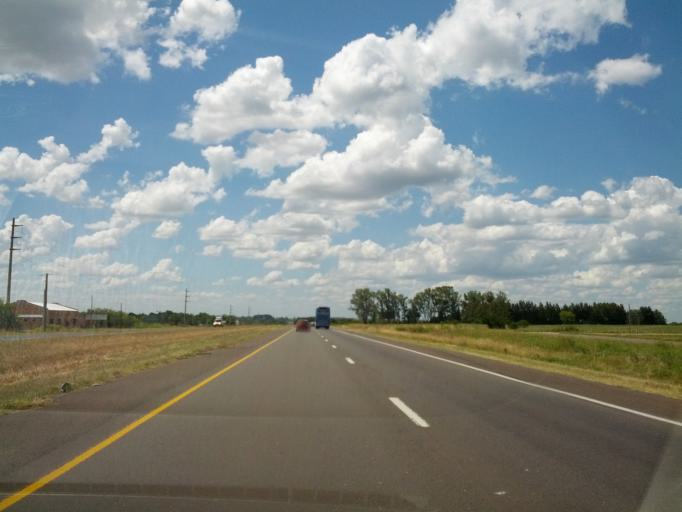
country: AR
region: Entre Rios
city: Concepcion del Uruguay
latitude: -32.4343
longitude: -58.2863
